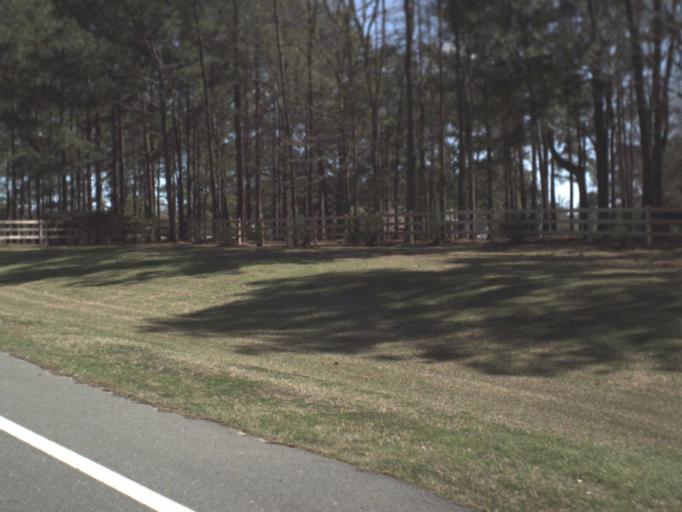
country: US
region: Florida
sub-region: Gadsden County
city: Chattahoochee
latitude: 30.7027
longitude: -84.7889
